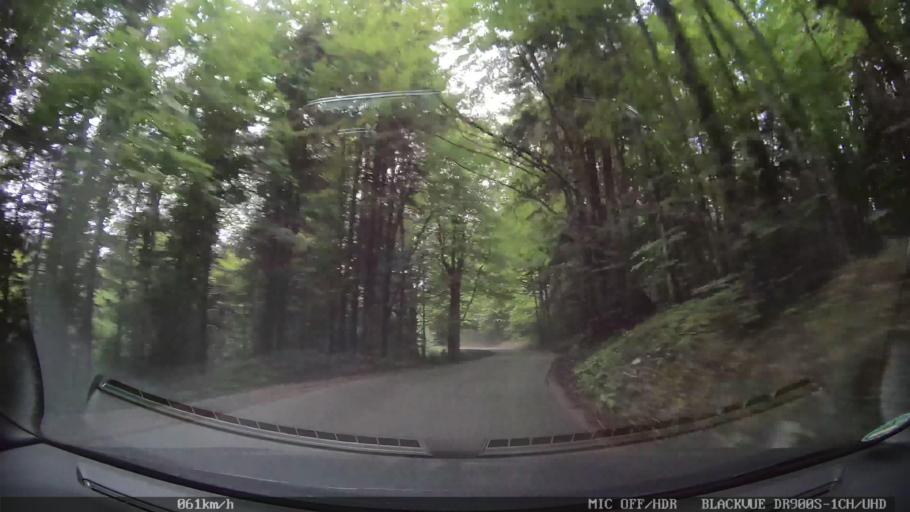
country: HR
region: Licko-Senjska
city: Jezerce
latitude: 44.9379
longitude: 15.5455
